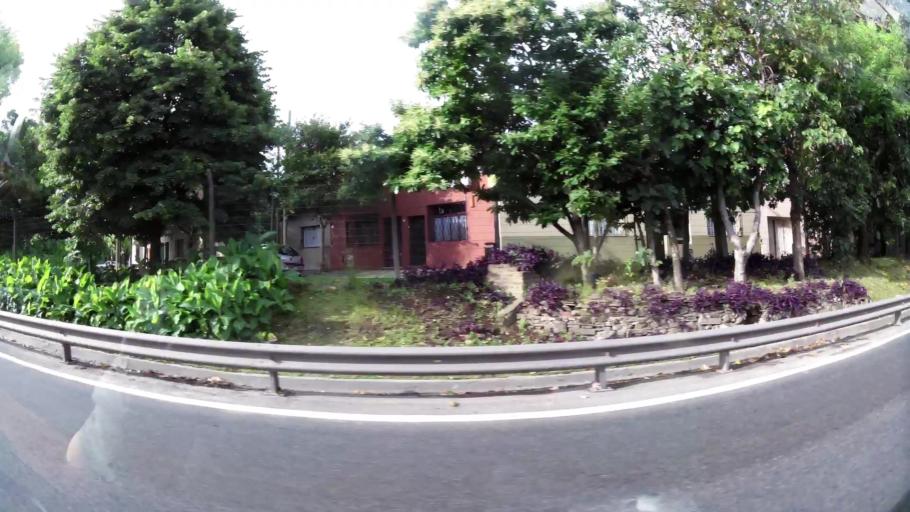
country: AR
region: Buenos Aires F.D.
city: Villa Lugano
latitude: -34.6490
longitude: -58.4742
